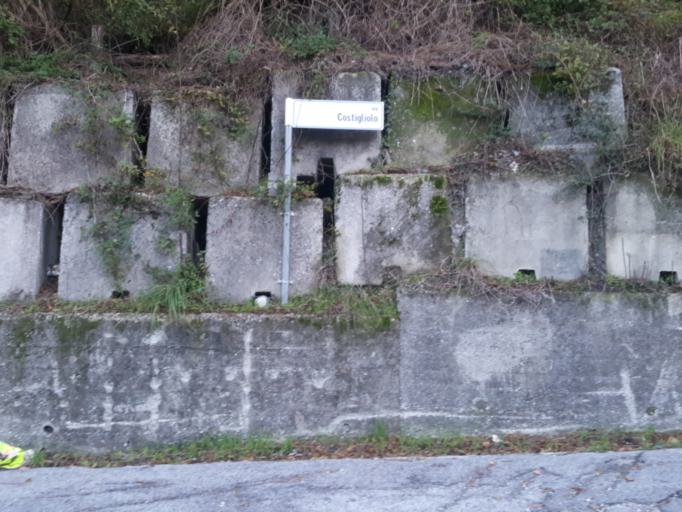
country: IT
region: Liguria
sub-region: Provincia di Genova
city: Mignanego
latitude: 44.5295
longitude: 8.9085
